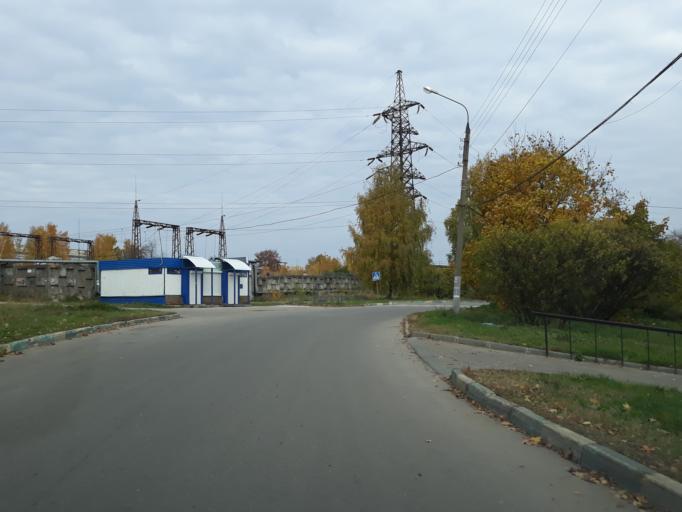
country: RU
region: Nizjnij Novgorod
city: Nizhniy Novgorod
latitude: 56.2371
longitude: 43.9772
